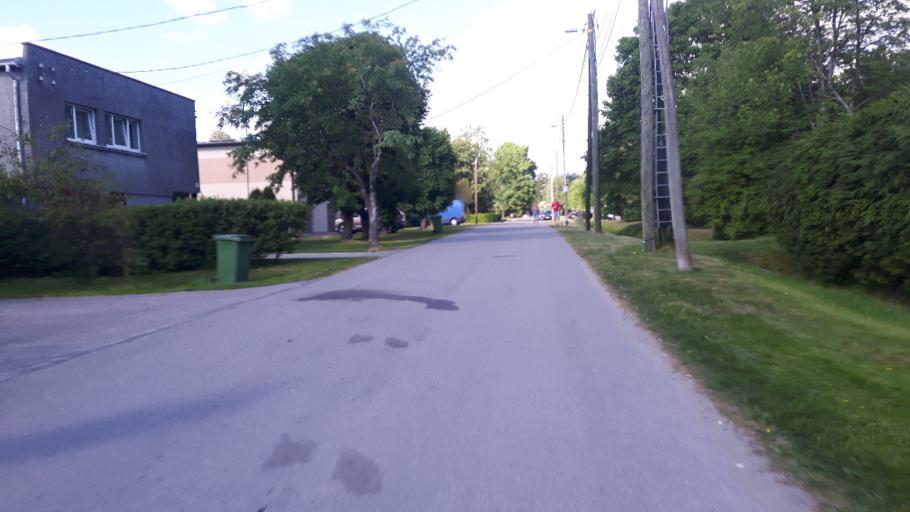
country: EE
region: Paernumaa
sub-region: Paikuse vald
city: Paikuse
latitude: 58.3494
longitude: 24.5712
